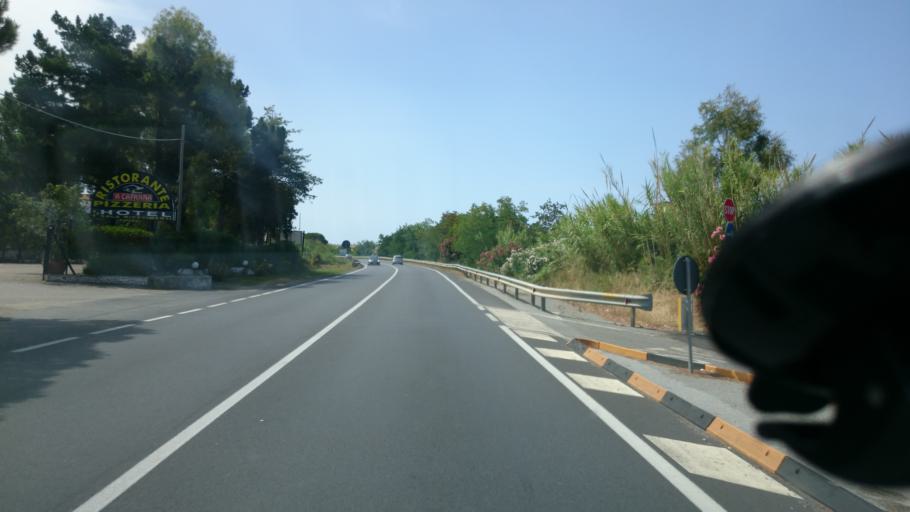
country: IT
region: Calabria
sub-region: Provincia di Cosenza
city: Diamante
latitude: 39.7012
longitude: 15.8140
